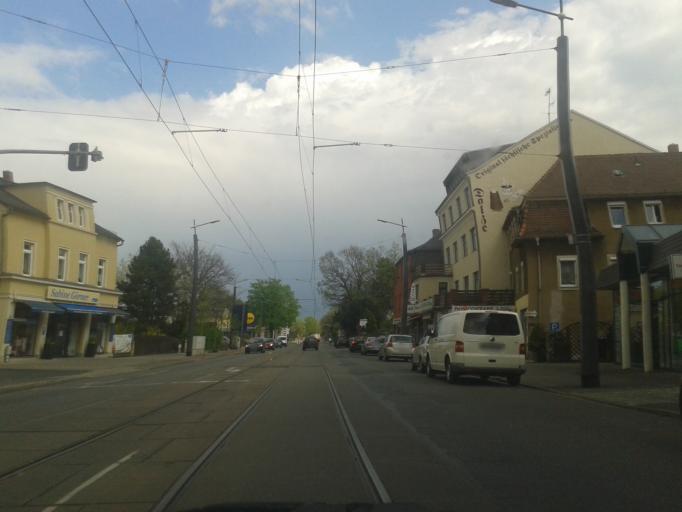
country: DE
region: Saxony
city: Radebeul
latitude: 51.1080
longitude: 13.6311
